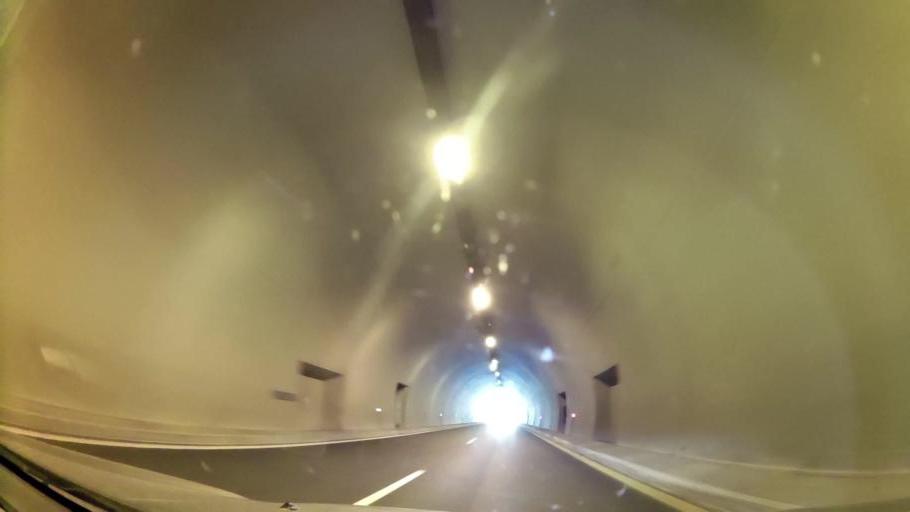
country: GR
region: Central Macedonia
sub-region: Nomos Imathias
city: Rizomata
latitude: 40.3810
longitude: 22.1067
